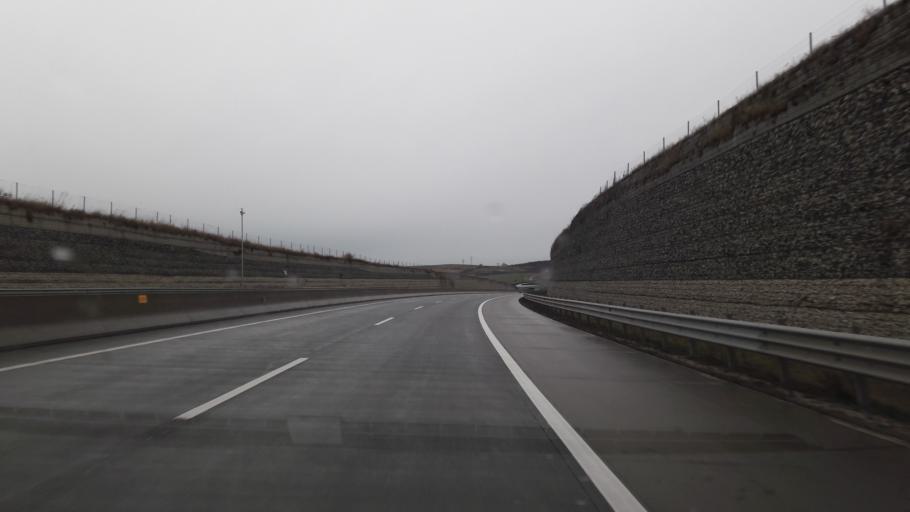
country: AT
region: Lower Austria
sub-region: Politischer Bezirk Mistelbach
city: Wolkersdorf im Weinviertel
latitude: 48.3858
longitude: 16.4929
